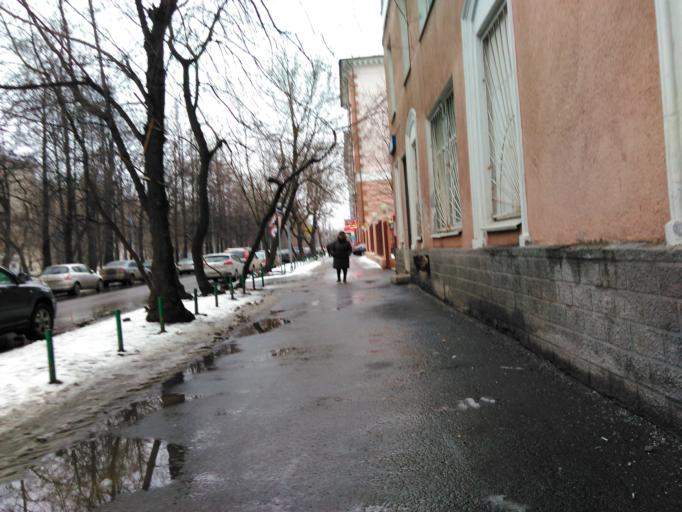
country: RU
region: Moscow
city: Nagornyy
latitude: 55.6617
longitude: 37.6252
